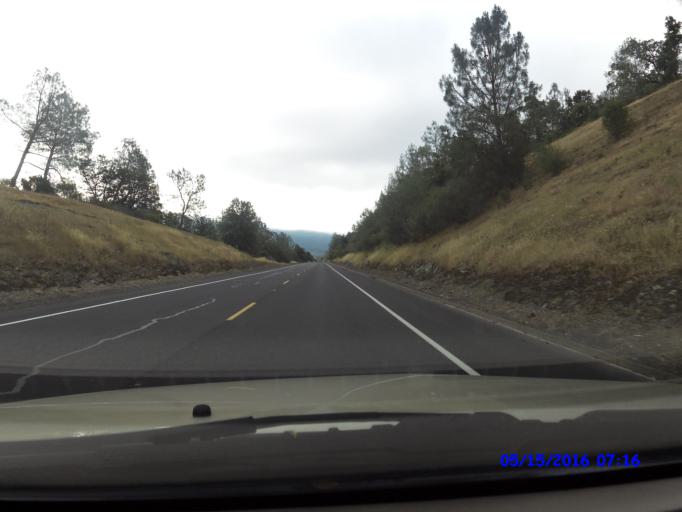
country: US
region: California
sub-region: Tuolumne County
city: East Sonora
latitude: 37.8203
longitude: -120.3258
